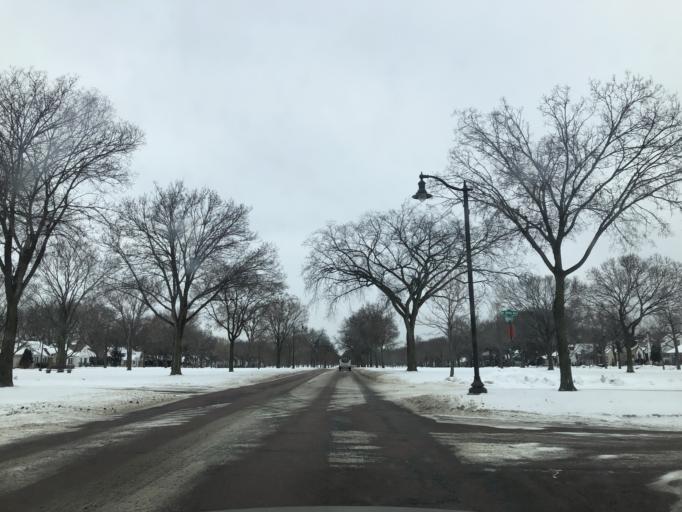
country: US
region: Minnesota
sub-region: Hennepin County
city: Robbinsdale
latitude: 45.0258
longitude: -93.3192
